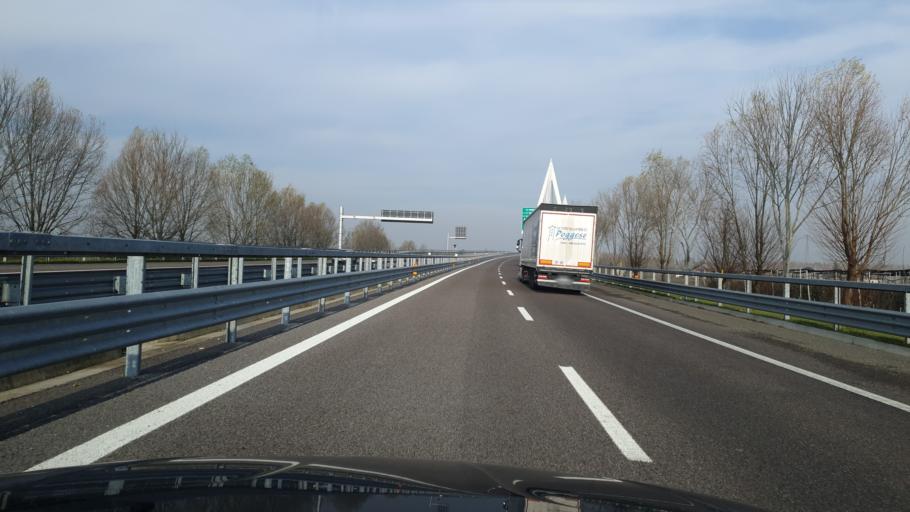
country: IT
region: Veneto
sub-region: Provincia di Padova
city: Piacenza d'Adige
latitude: 45.1135
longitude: 11.5293
